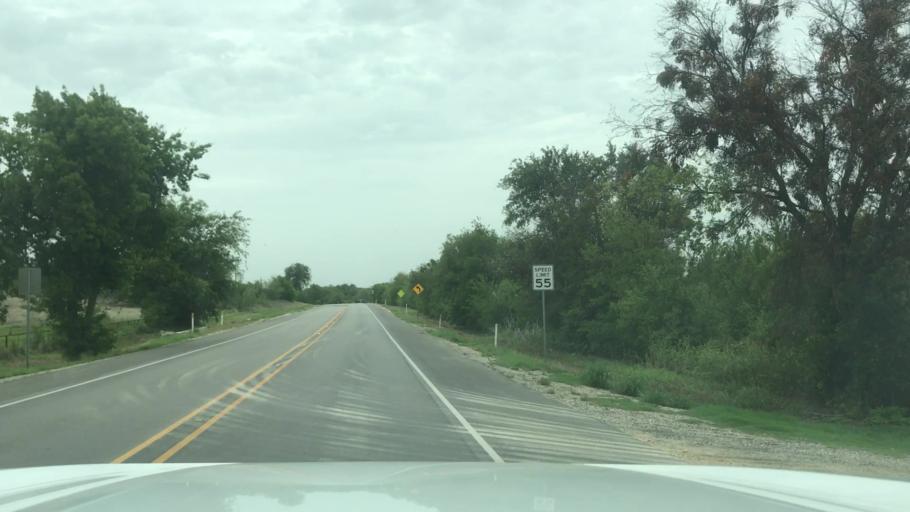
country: US
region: Texas
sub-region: Erath County
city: Dublin
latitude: 32.0622
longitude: -98.2133
